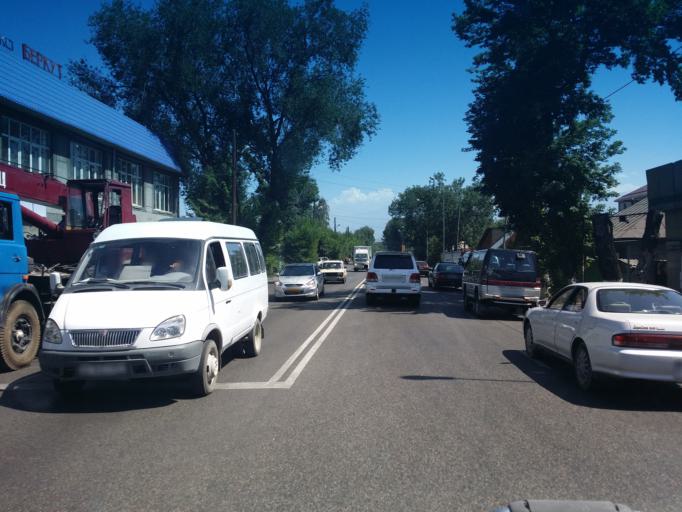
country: KZ
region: Almaty Oblysy
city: Pervomayskiy
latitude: 43.3547
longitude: 76.9491
